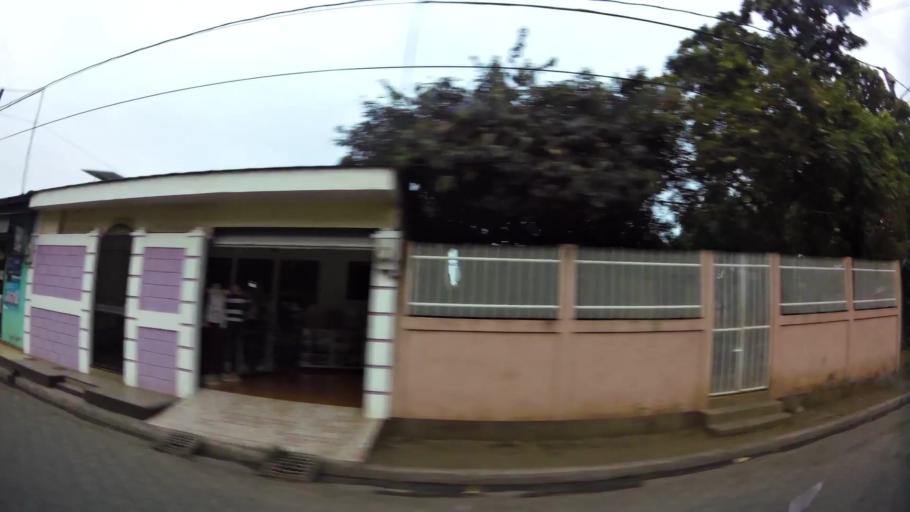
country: NI
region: Masaya
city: Nindiri
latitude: 12.0058
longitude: -86.1198
